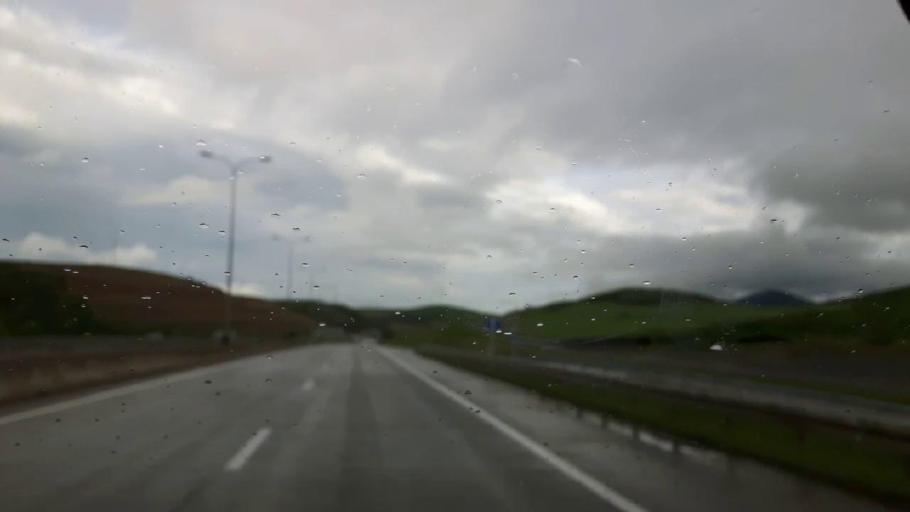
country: GE
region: Shida Kartli
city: Kaspi
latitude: 41.9997
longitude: 44.3894
